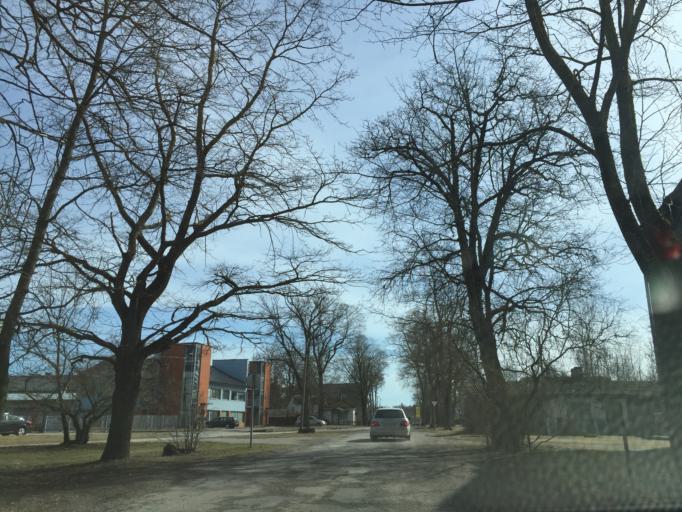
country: EE
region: Paernumaa
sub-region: Paernu linn
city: Parnu
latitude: 58.3836
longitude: 24.5262
